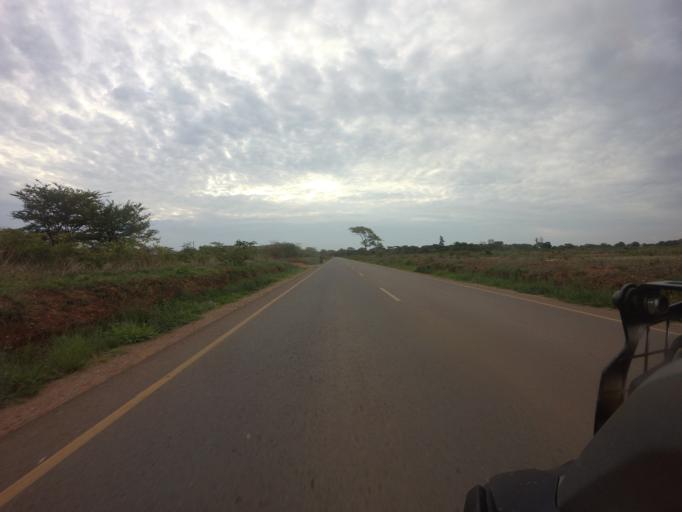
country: ZM
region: Lusaka
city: Lusaka
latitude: -15.5157
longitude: 28.2157
